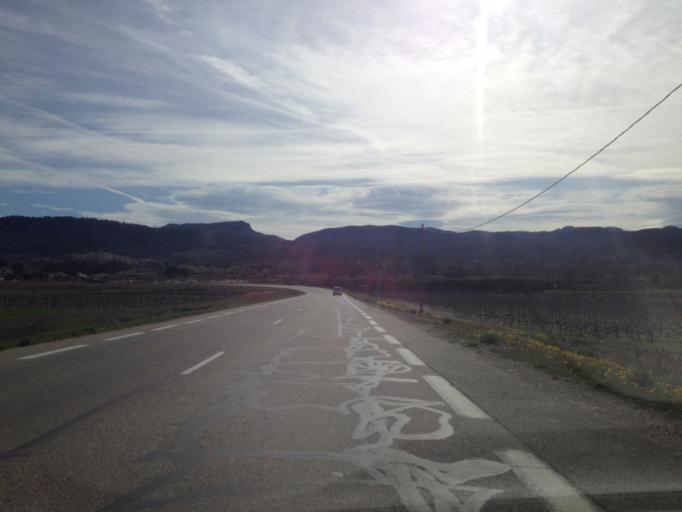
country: FR
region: Provence-Alpes-Cote d'Azur
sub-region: Departement du Vaucluse
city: Sablet
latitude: 44.1930
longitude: 4.9883
